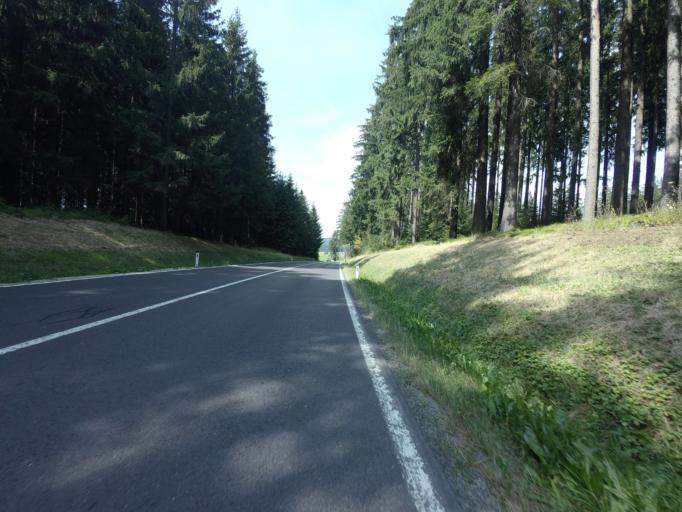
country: AT
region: Upper Austria
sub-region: Politischer Bezirk Urfahr-Umgebung
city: Schenkenfelden
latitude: 48.5201
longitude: 14.3333
